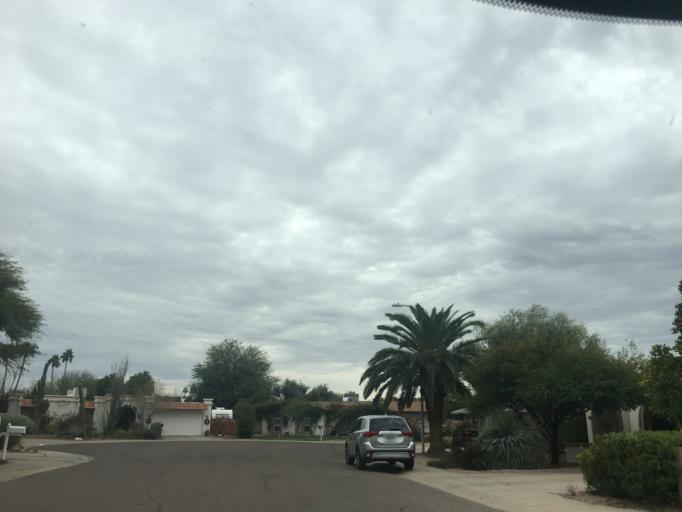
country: US
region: Arizona
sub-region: Maricopa County
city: Tempe
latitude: 33.3690
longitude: -111.9161
